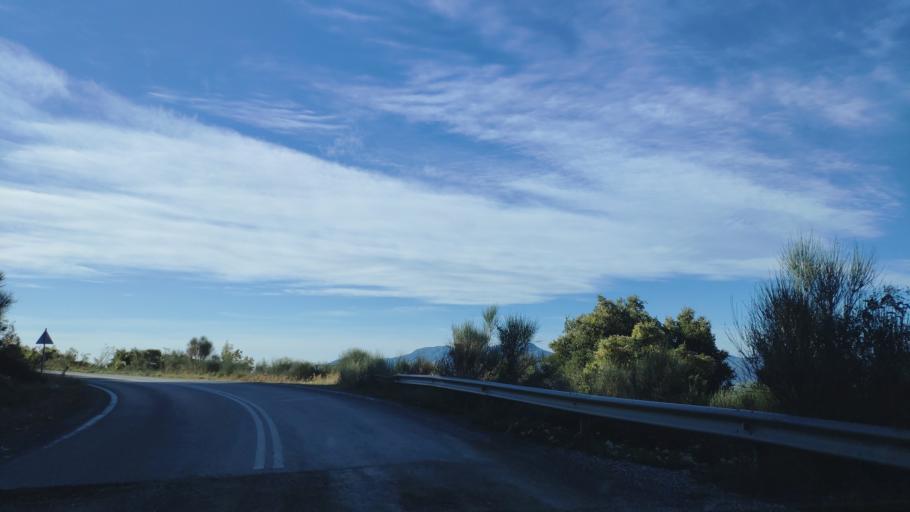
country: GR
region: Peloponnese
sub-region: Nomos Arkadias
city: Dimitsana
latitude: 37.5678
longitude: 22.0604
